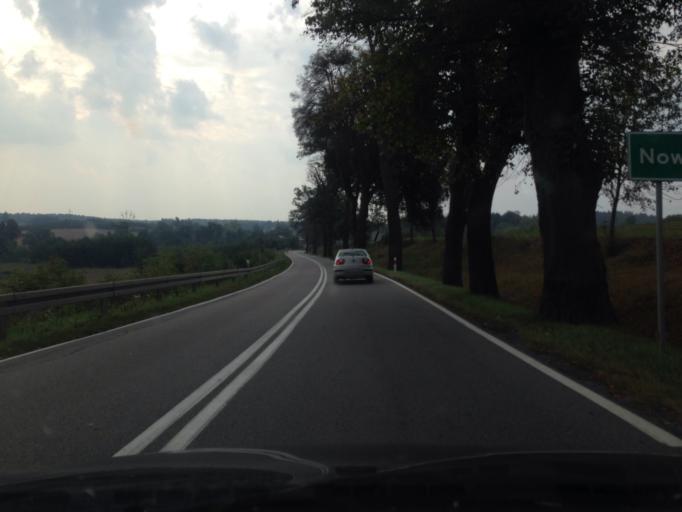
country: PL
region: Pomeranian Voivodeship
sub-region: Powiat sztumski
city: Sztum
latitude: 53.8815
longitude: 19.0072
